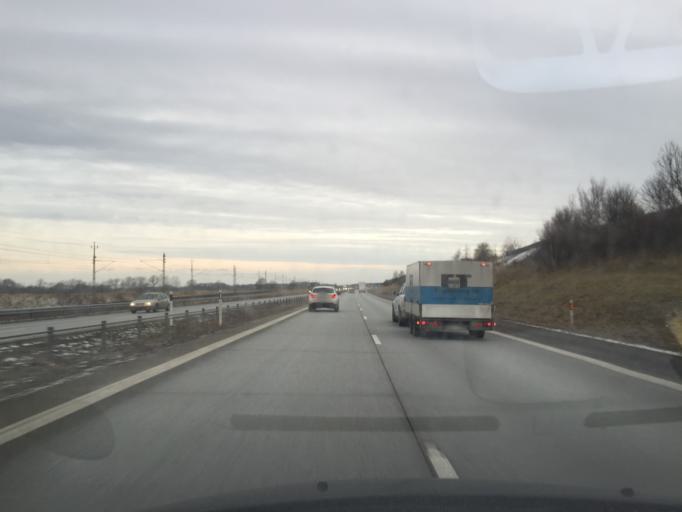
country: SE
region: Halland
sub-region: Falkenbergs Kommun
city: Falkenberg
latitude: 56.9664
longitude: 12.4438
